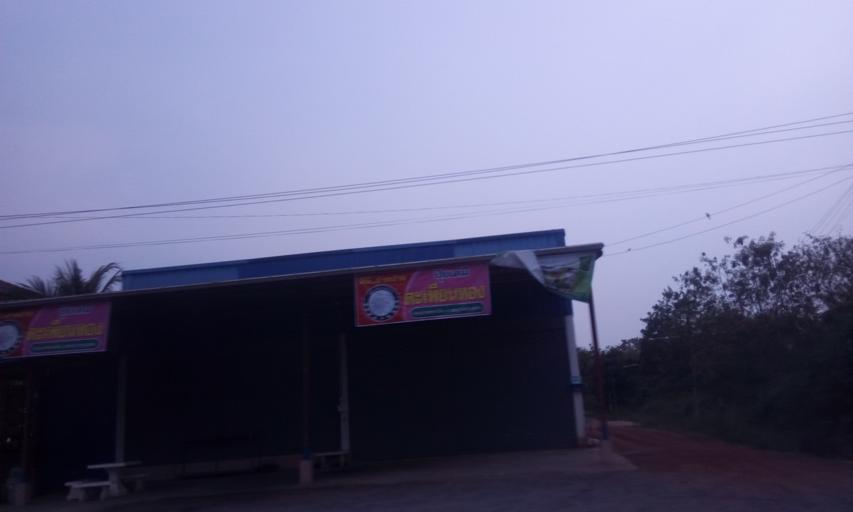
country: TH
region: Bangkok
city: Nong Chok
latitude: 13.8562
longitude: 100.8744
